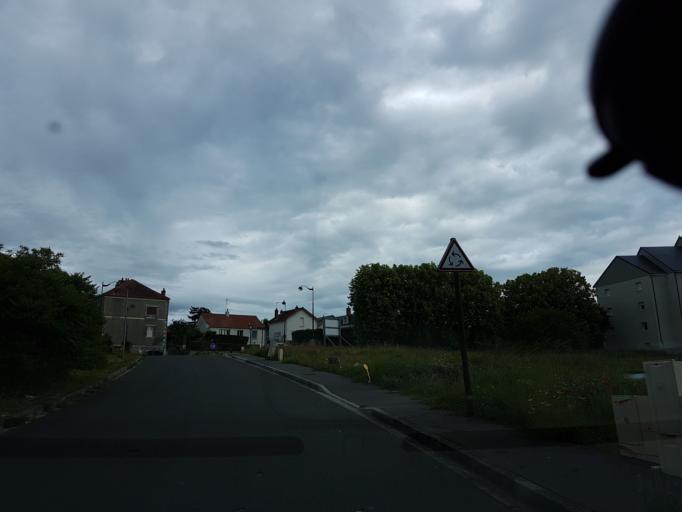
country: FR
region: Centre
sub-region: Departement du Cher
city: Bourges
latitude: 47.0950
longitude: 2.4080
